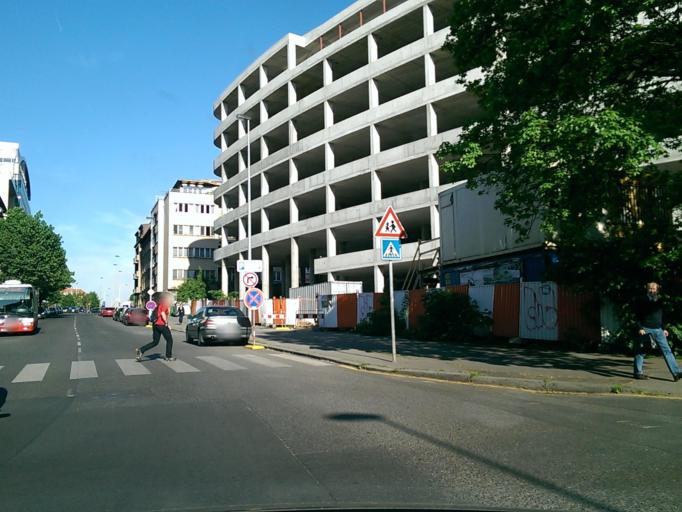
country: CZ
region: Praha
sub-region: Praha 2
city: Vysehrad
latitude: 50.0568
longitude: 14.4307
